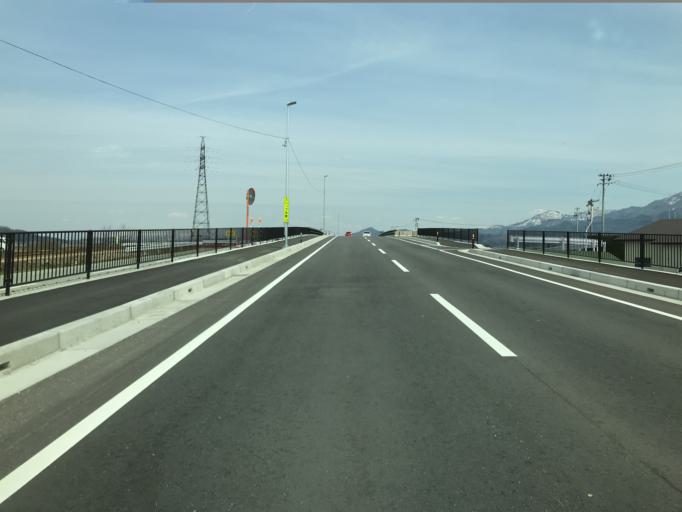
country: JP
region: Yamagata
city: Higashine
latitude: 38.4500
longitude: 140.3568
